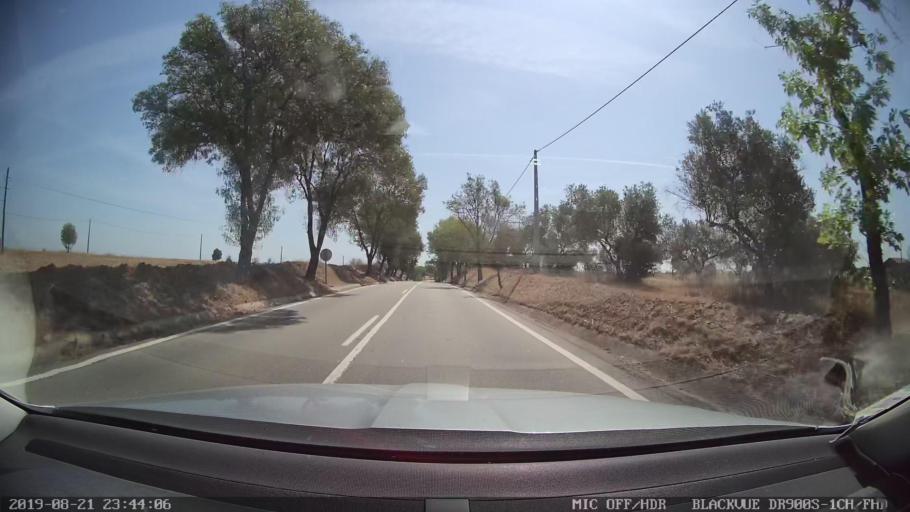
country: PT
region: Castelo Branco
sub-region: Idanha-A-Nova
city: Idanha-a-Nova
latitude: 39.8475
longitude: -7.2840
